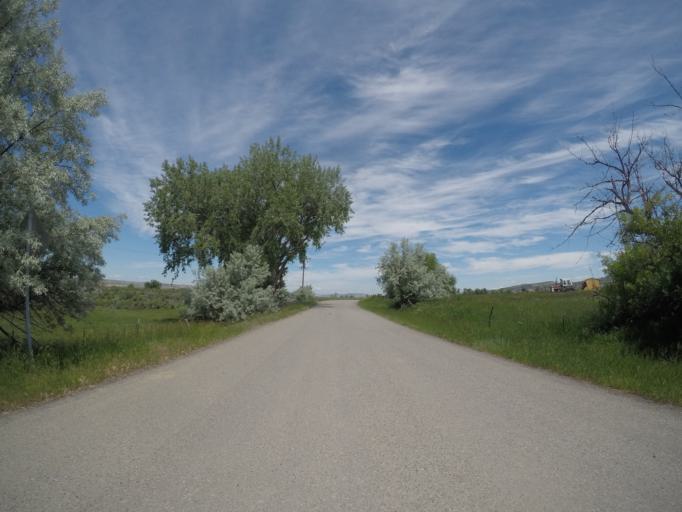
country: US
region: Montana
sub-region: Carbon County
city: Red Lodge
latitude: 45.2476
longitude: -108.8833
